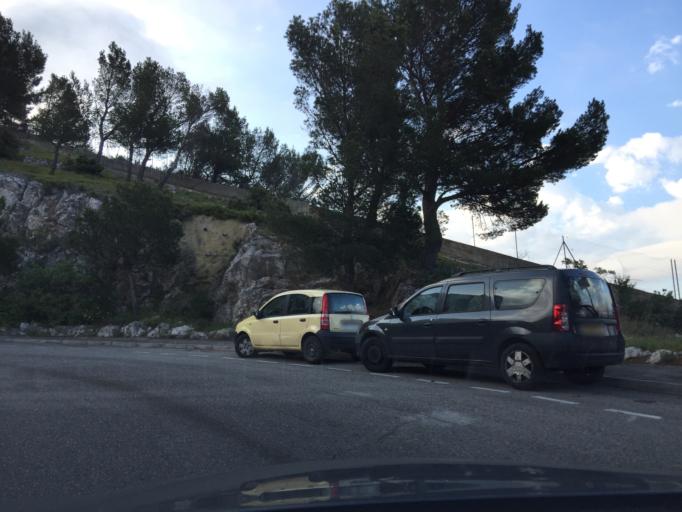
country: FR
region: Provence-Alpes-Cote d'Azur
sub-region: Departement des Bouches-du-Rhone
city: Marseille 09
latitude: 43.2496
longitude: 5.4246
